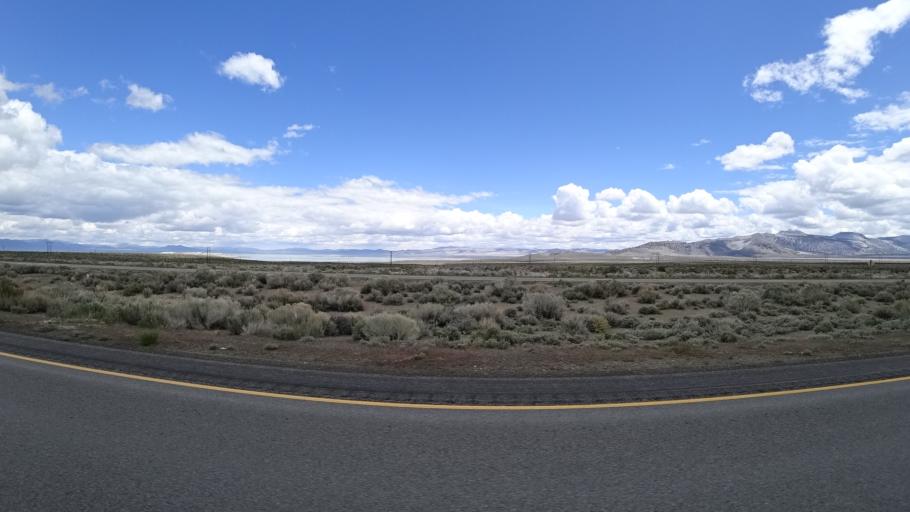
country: US
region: California
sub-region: Mono County
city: Mammoth Lakes
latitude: 37.9355
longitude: -119.1015
